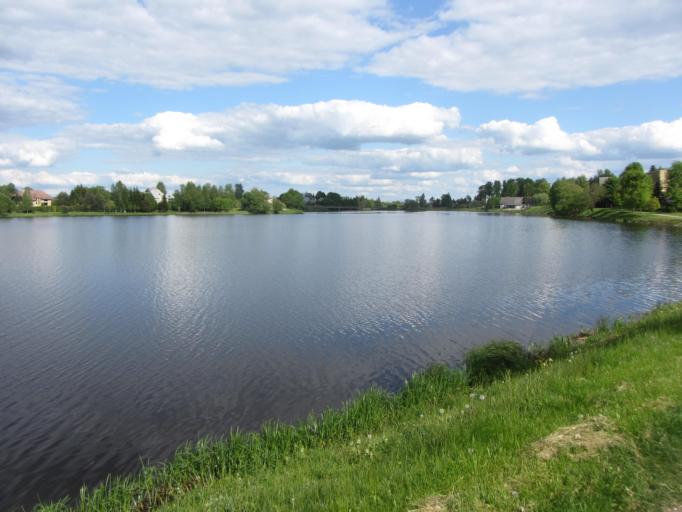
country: LT
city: Sirvintos
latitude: 55.0410
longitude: 24.9588
